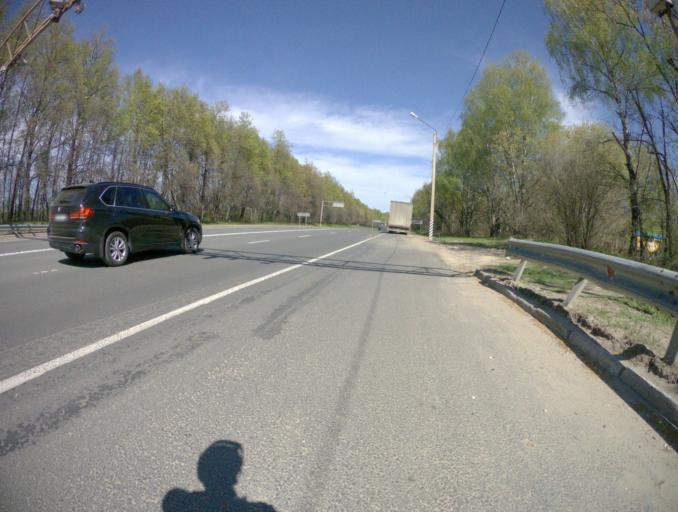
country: RU
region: Vladimir
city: Bogolyubovo
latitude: 56.1771
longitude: 40.5012
